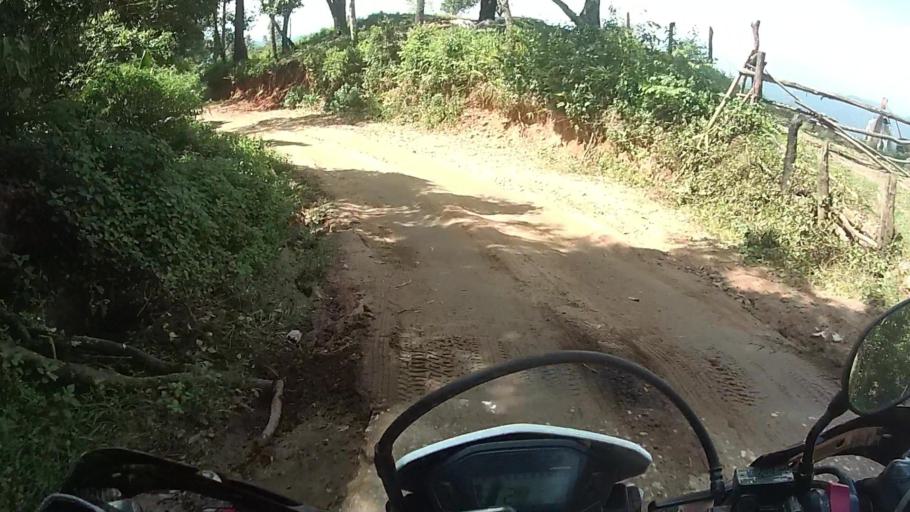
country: TH
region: Chiang Mai
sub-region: Amphoe Chiang Dao
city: Chiang Dao
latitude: 19.3242
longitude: 98.8290
